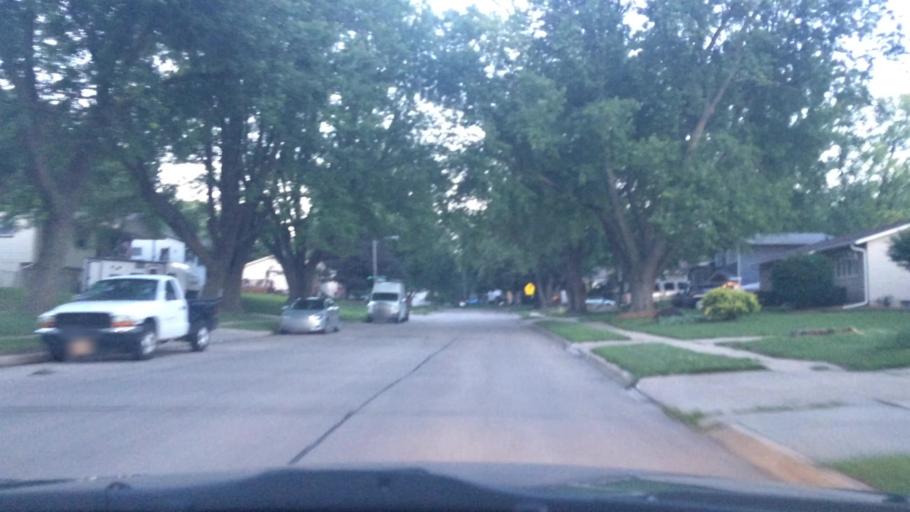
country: US
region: Nebraska
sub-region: Sarpy County
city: La Vista
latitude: 41.1850
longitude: -96.0482
